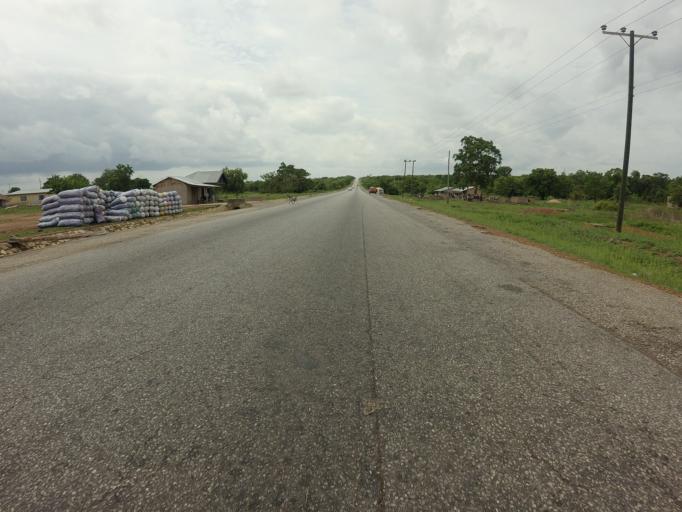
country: GH
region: Brong-Ahafo
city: Kintampo
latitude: 8.6652
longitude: -1.5189
